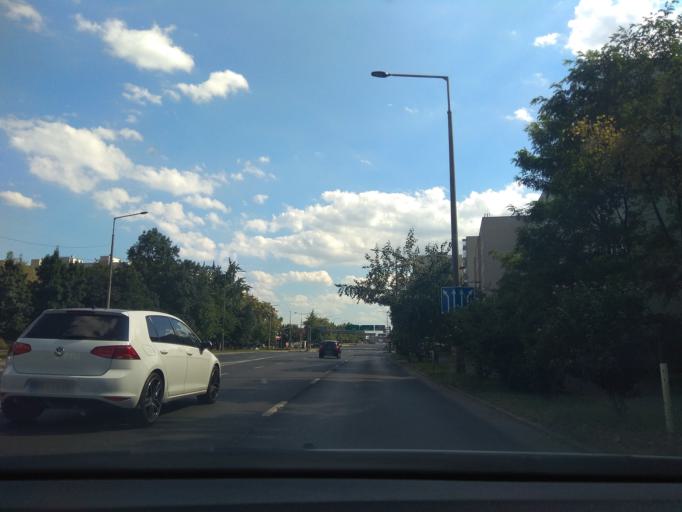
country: HU
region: Borsod-Abauj-Zemplen
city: Miskolc
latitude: 48.1012
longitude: 20.7920
